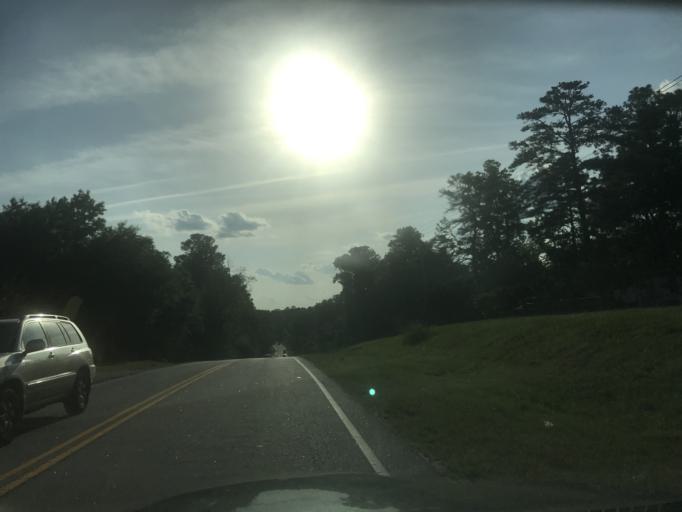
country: US
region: North Carolina
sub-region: Wake County
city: Knightdale
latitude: 35.7545
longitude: -78.5261
